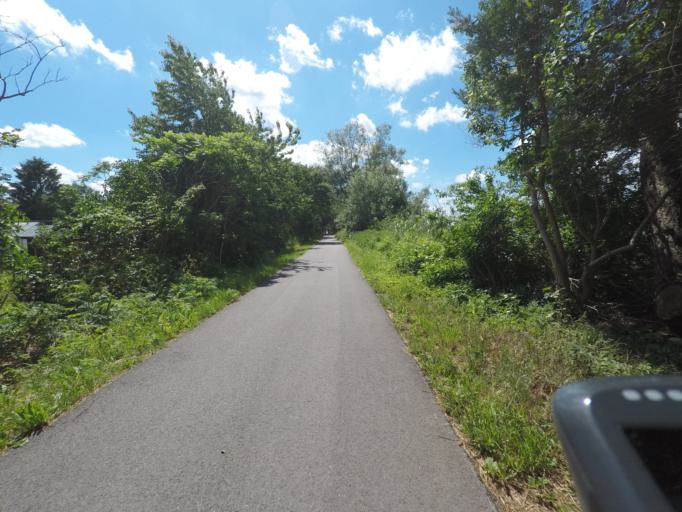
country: DE
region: Hamburg
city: Bergedorf
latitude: 53.4430
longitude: 10.2173
